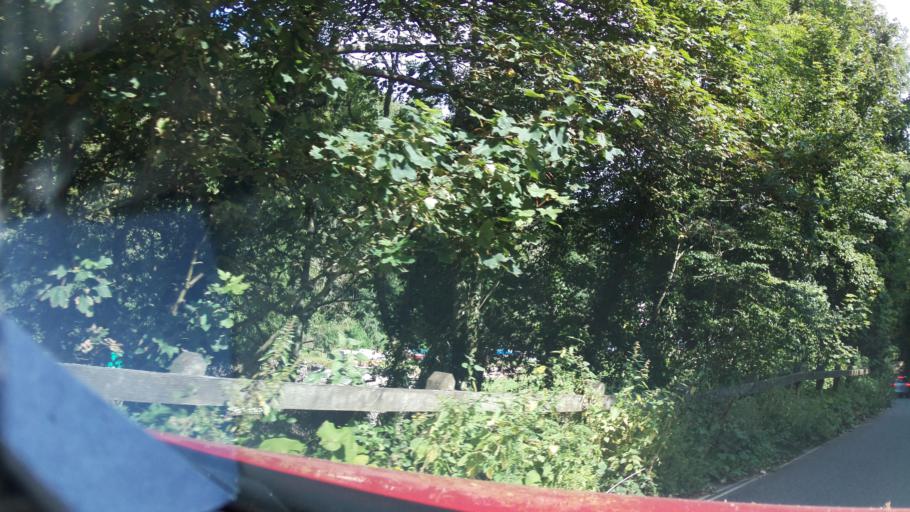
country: GB
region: England
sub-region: Devon
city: Dartmouth
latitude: 50.3525
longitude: -3.5643
